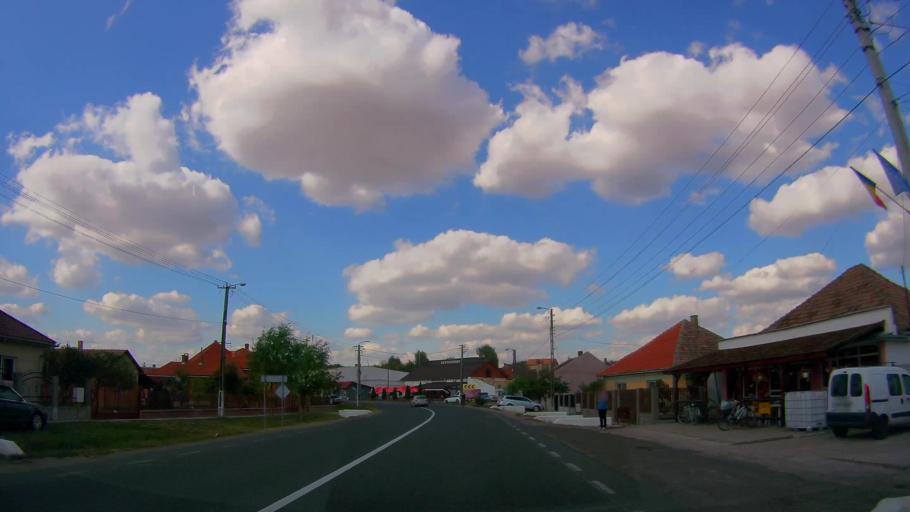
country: RO
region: Satu Mare
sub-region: Oras Ardud
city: Ardud
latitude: 47.6495
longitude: 22.8913
